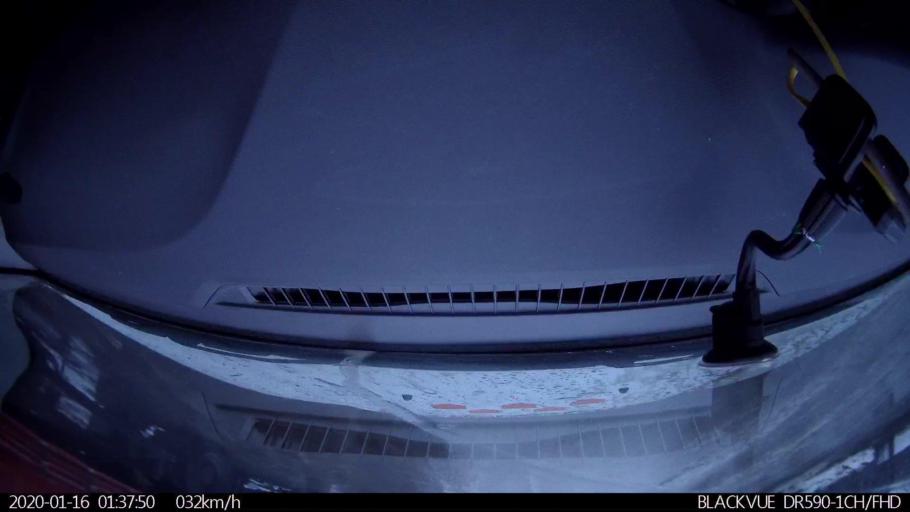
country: RU
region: Nizjnij Novgorod
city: Gorbatovka
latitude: 56.3401
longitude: 43.8060
